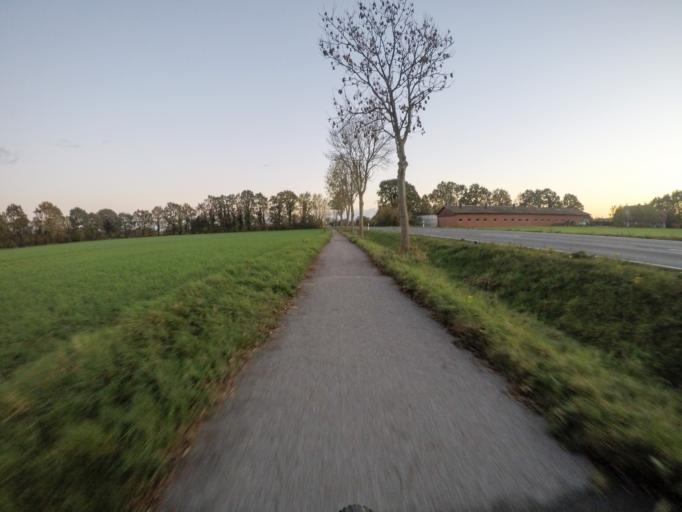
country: DE
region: North Rhine-Westphalia
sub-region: Regierungsbezirk Dusseldorf
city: Bocholt
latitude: 51.8221
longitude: 6.5618
